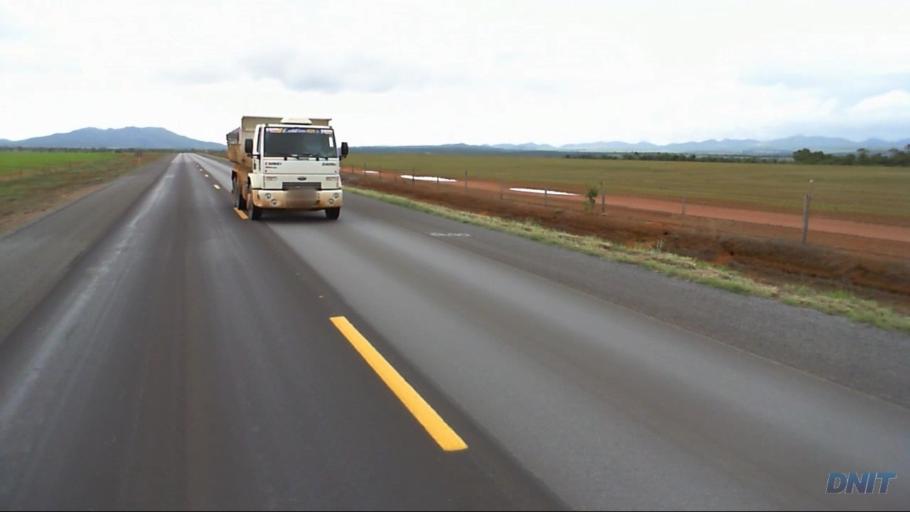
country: BR
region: Goias
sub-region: Padre Bernardo
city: Padre Bernardo
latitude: -15.2194
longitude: -48.6335
